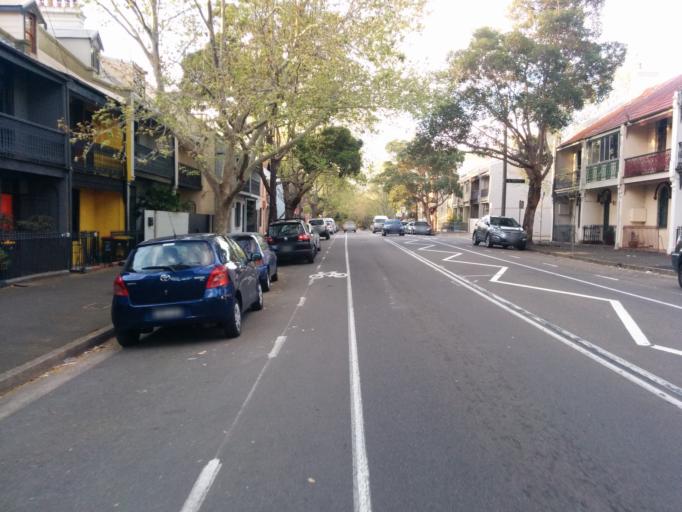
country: AU
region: New South Wales
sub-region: City of Sydney
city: Redfern
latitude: -33.8877
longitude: 151.2120
